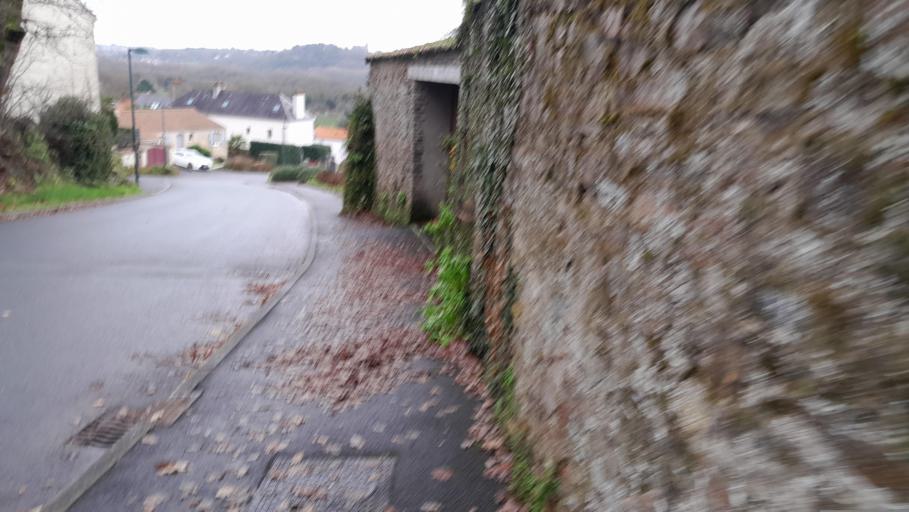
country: FR
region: Pays de la Loire
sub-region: Departement de la Loire-Atlantique
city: Oudon
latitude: 47.3483
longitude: -1.2850
